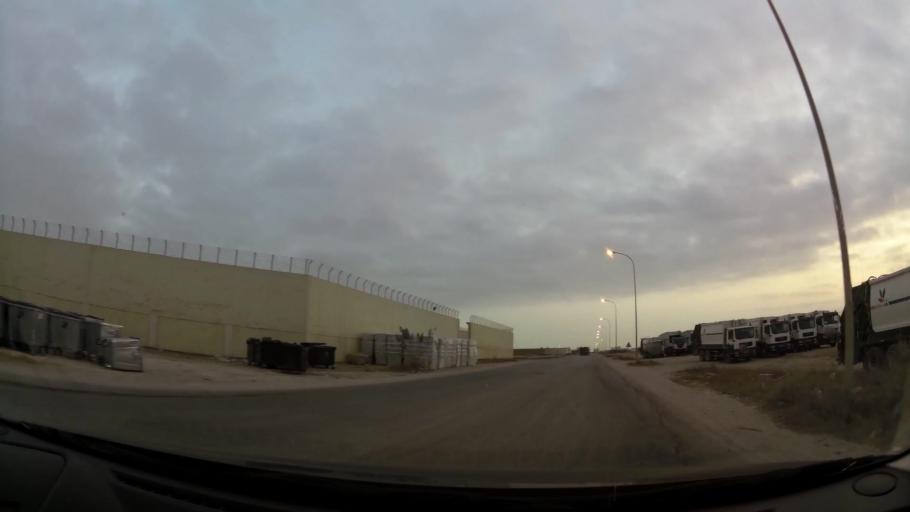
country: OM
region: Zufar
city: Salalah
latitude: 17.0356
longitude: 54.0423
